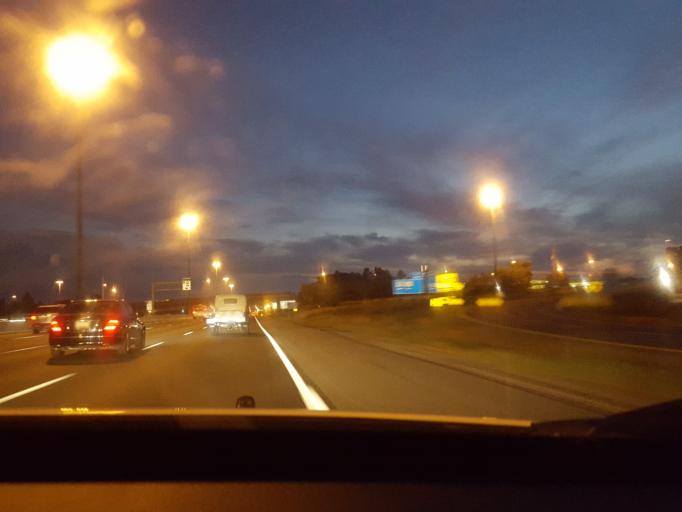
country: CA
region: Ontario
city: Oakville
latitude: 43.4638
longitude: -79.6814
